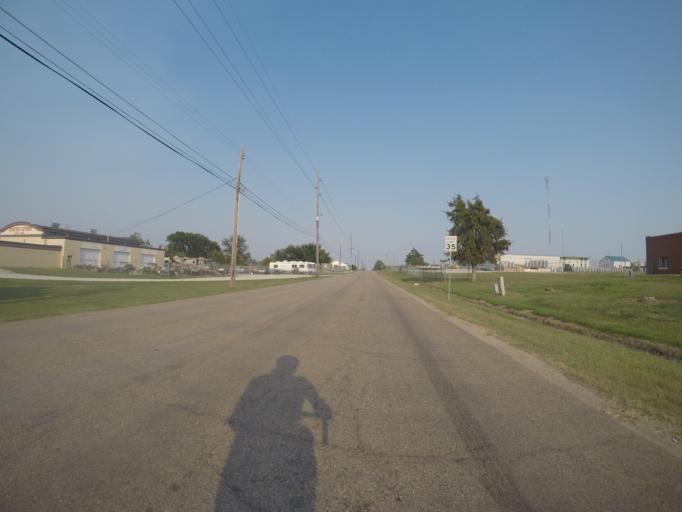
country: US
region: Nebraska
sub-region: Gage County
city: Beatrice
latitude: 40.2629
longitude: -96.7842
